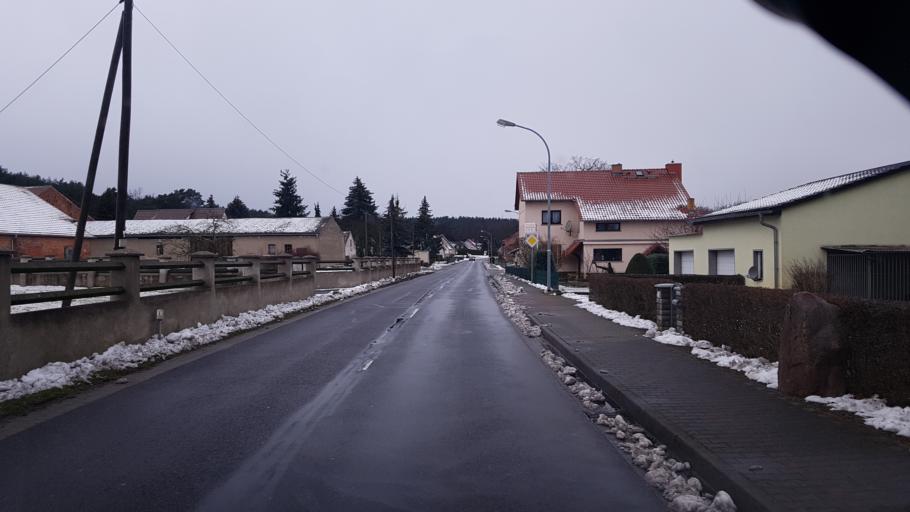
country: DE
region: Brandenburg
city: Schenkendobern
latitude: 51.9703
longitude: 14.5718
